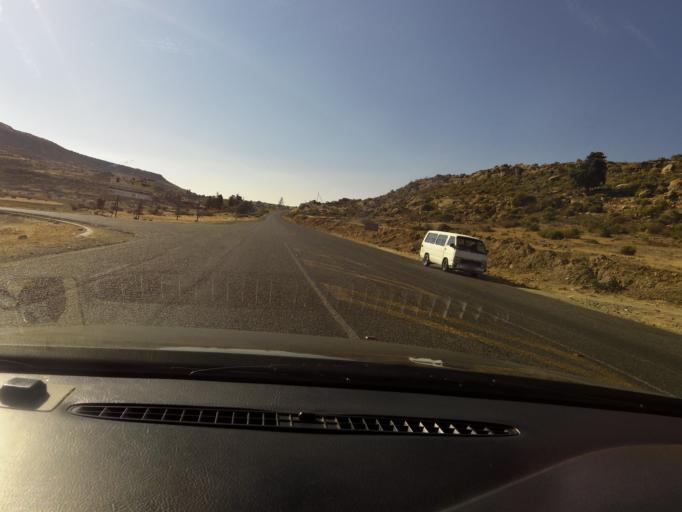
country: LS
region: Mohale's Hoek District
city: Mohale's Hoek
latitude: -30.0837
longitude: 27.4290
